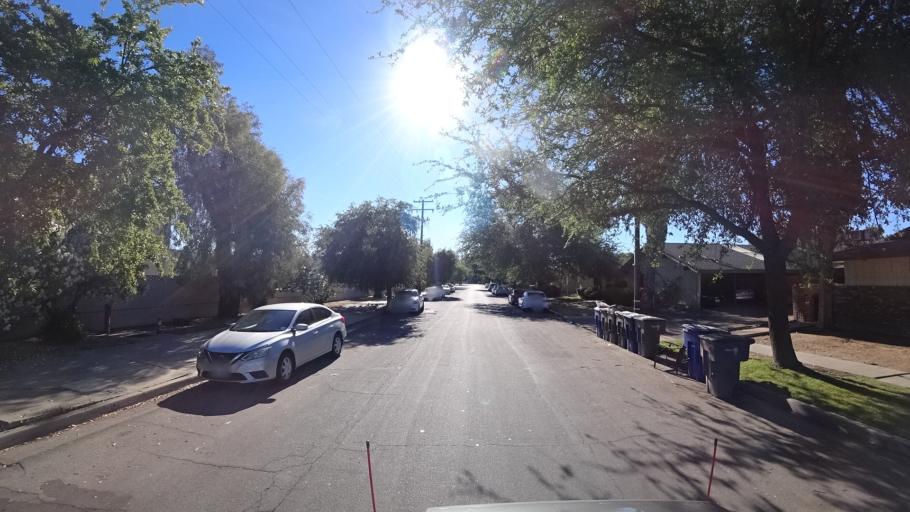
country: US
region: California
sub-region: Fresno County
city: Fresno
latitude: 36.8070
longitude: -119.8290
